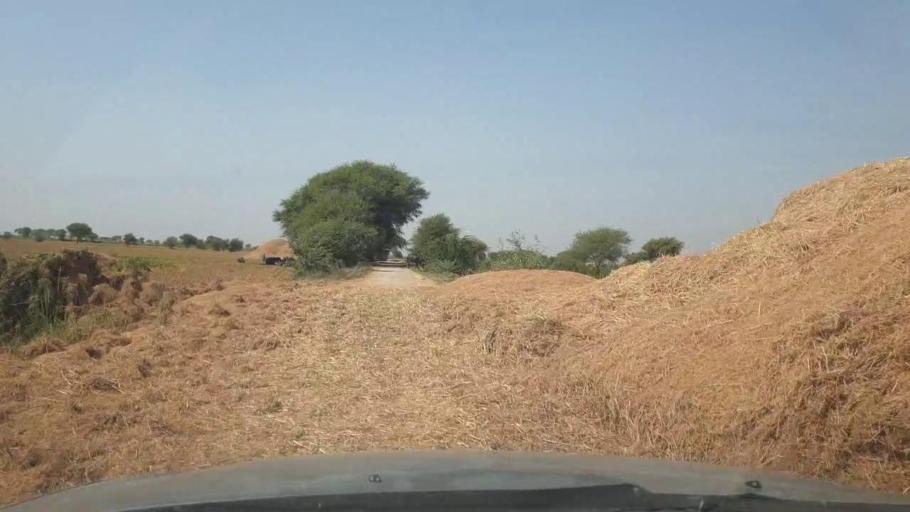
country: PK
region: Sindh
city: Bulri
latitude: 24.8720
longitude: 68.4488
